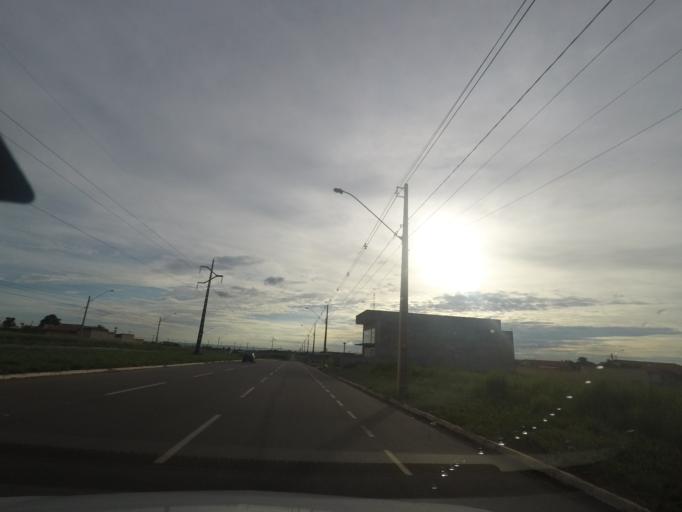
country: BR
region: Goias
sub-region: Trindade
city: Trindade
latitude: -16.7209
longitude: -49.3980
